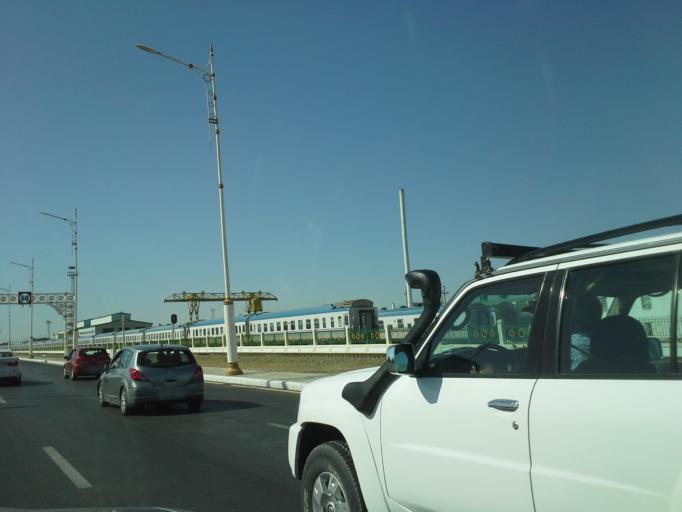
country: TM
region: Ahal
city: Ashgabat
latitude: 37.9330
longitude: 58.4147
